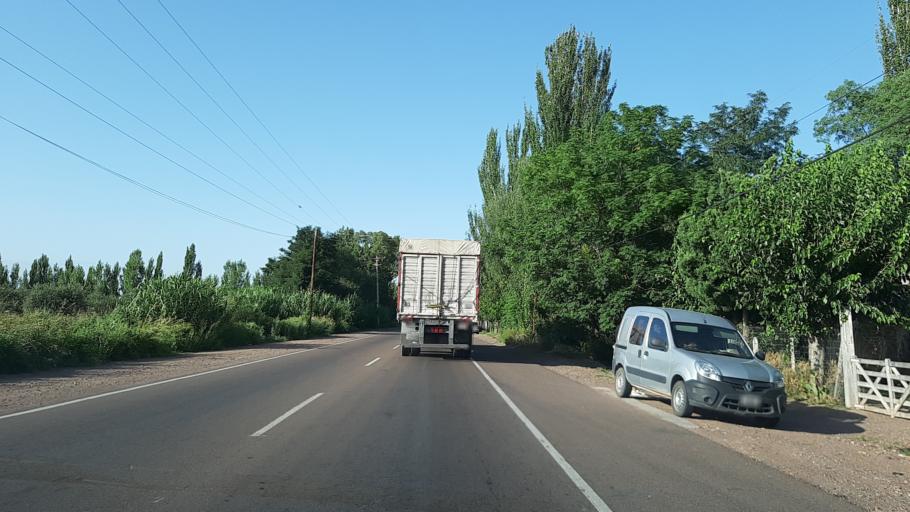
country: AR
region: Mendoza
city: San Martin
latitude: -33.0356
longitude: -68.5152
